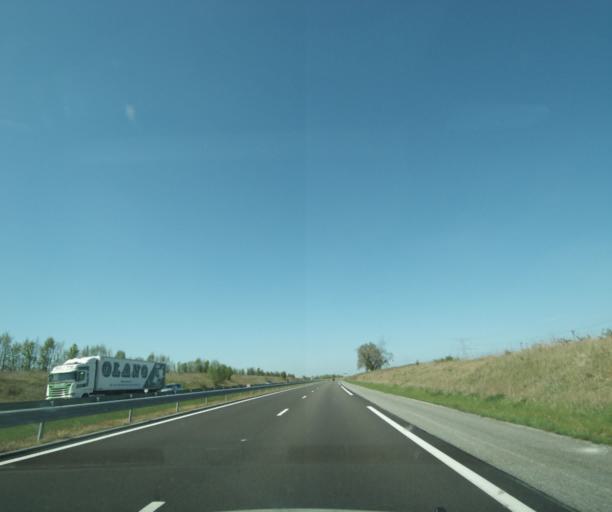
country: FR
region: Bourgogne
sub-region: Departement de la Nievre
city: Neuvy-sur-Loire
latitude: 47.5563
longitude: 2.8839
